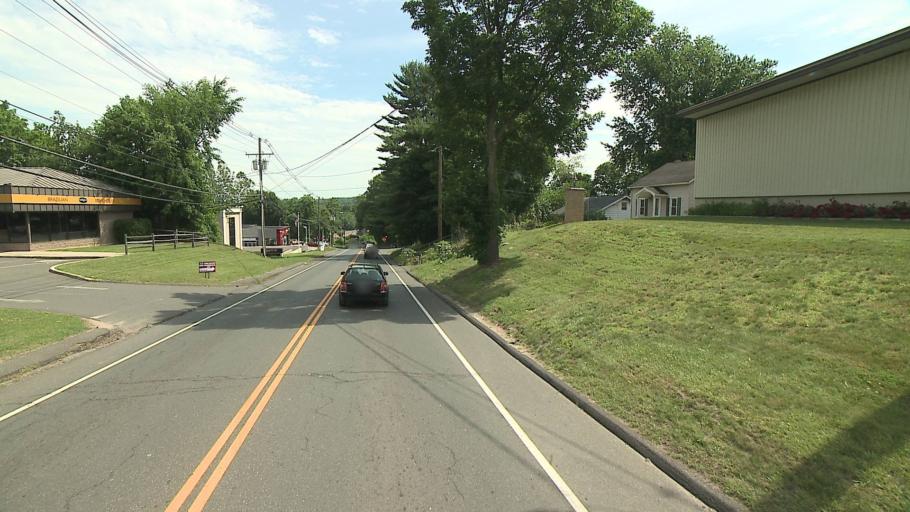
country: US
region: Connecticut
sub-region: Fairfield County
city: Danbury
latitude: 41.4029
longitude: -73.4241
